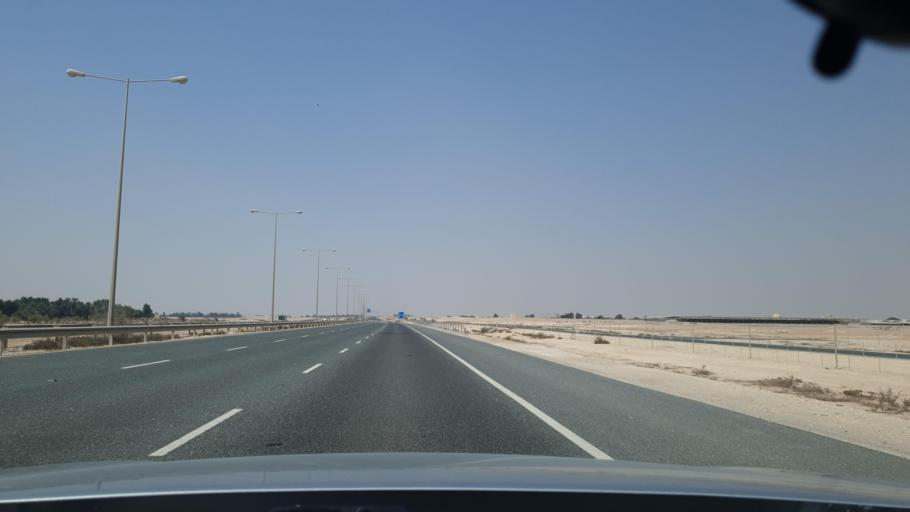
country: QA
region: Al Khawr
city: Al Khawr
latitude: 25.7776
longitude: 51.4069
